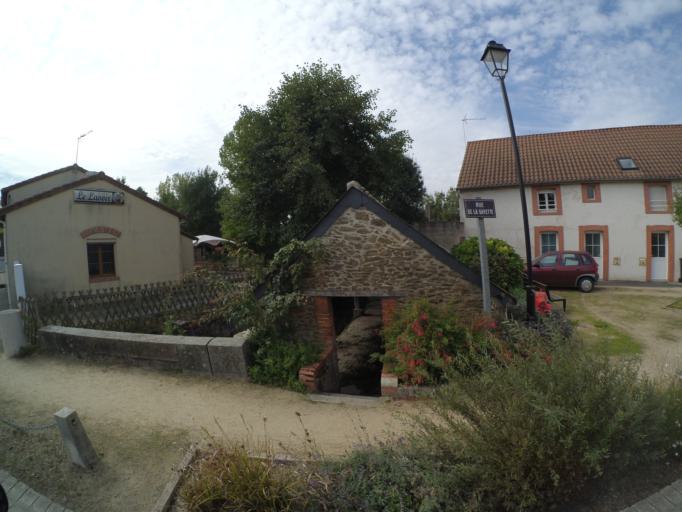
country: FR
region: Pays de la Loire
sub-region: Departement de Maine-et-Loire
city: Saint-Lambert-du-Lattay
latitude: 47.2166
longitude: -0.6068
